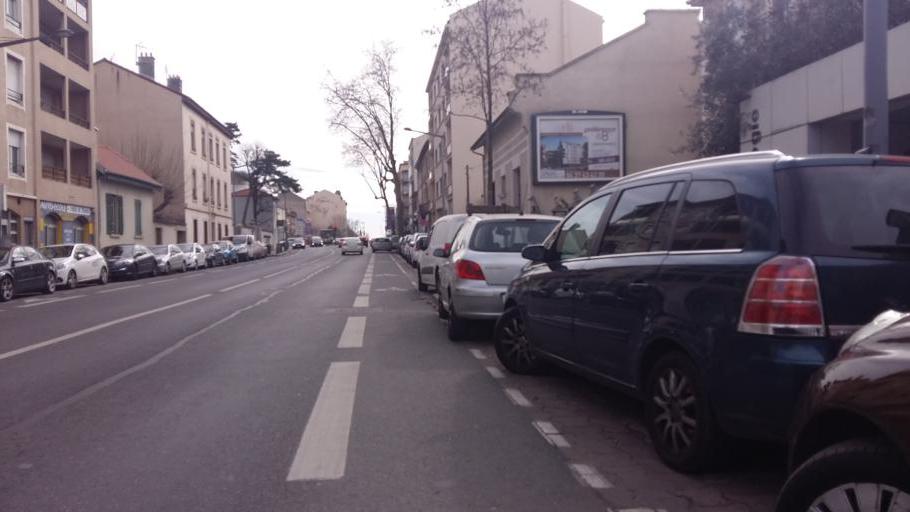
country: FR
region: Rhone-Alpes
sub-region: Departement du Rhone
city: Lyon
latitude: 45.7311
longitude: 4.8536
